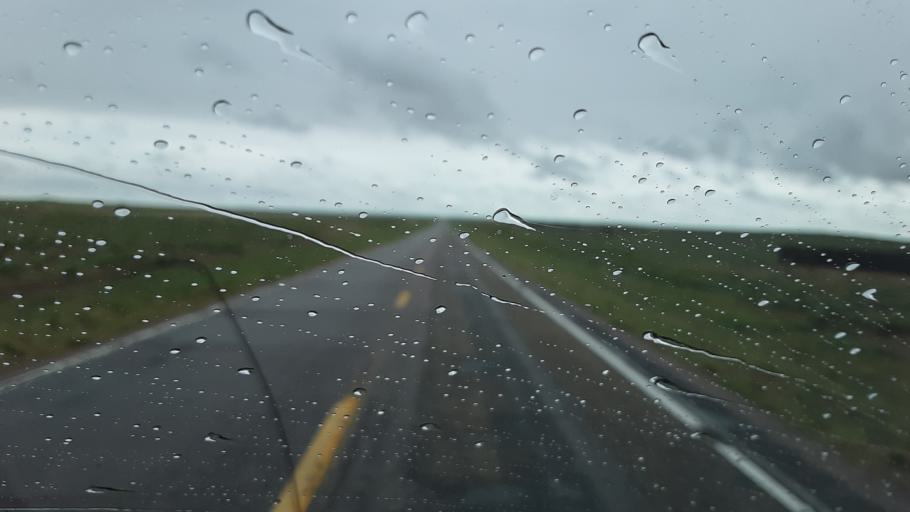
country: US
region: Colorado
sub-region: Lincoln County
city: Hugo
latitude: 38.8494
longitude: -103.2804
